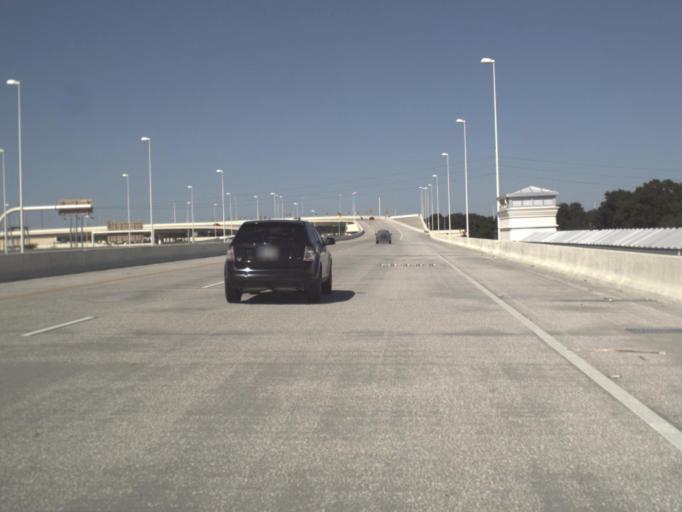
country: US
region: Florida
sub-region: Hillsborough County
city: Tampa
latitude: 27.9599
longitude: -82.4255
